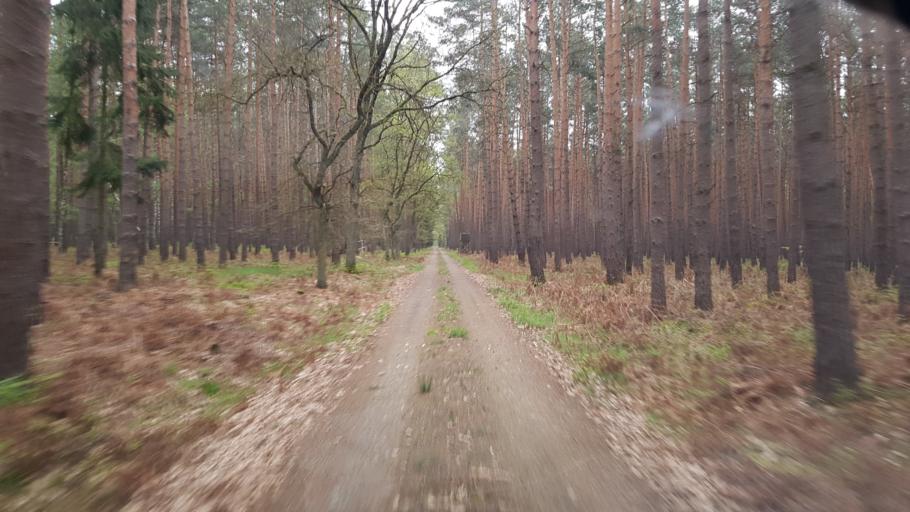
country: DE
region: Brandenburg
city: Schonewalde
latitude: 51.7144
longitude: 13.5486
